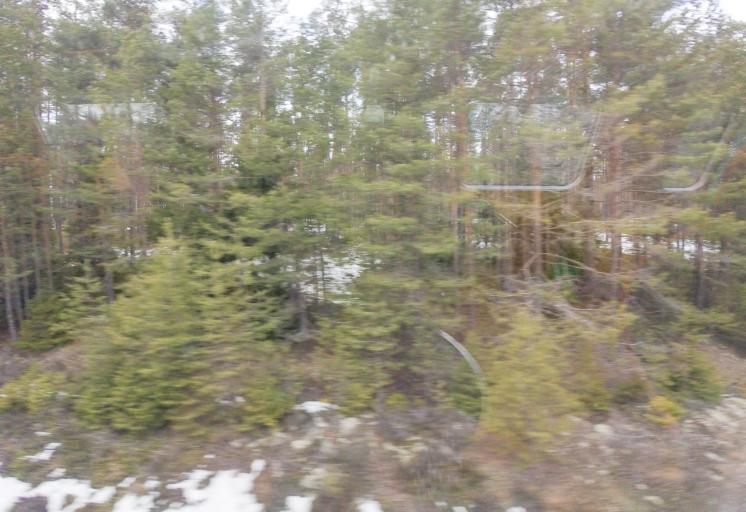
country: FI
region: South Karelia
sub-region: Lappeenranta
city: Lemi
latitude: 60.9860
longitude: 27.9245
